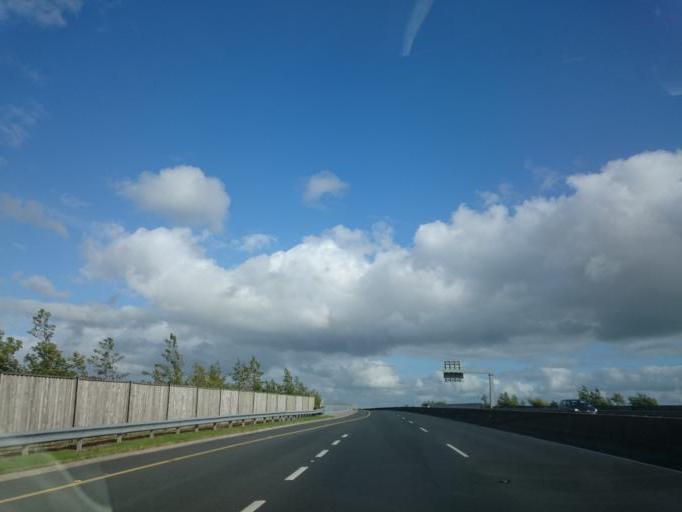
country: IE
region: Connaught
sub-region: County Galway
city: Athenry
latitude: 53.2839
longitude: -8.7534
